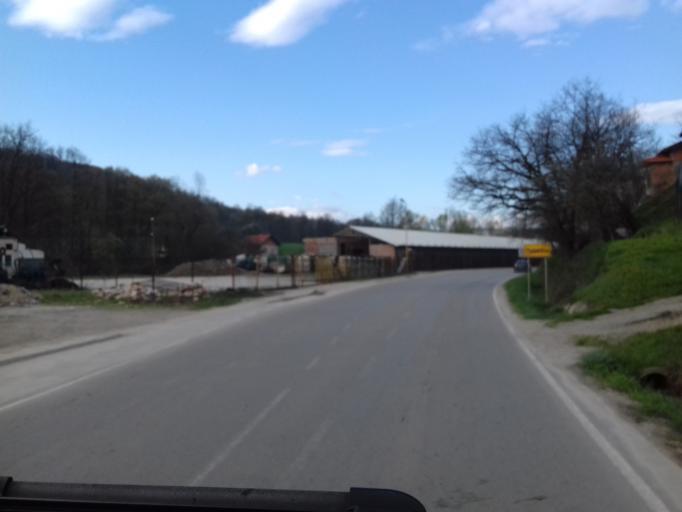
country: BA
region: Federation of Bosnia and Herzegovina
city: Tesanjka
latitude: 44.6369
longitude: 18.0123
